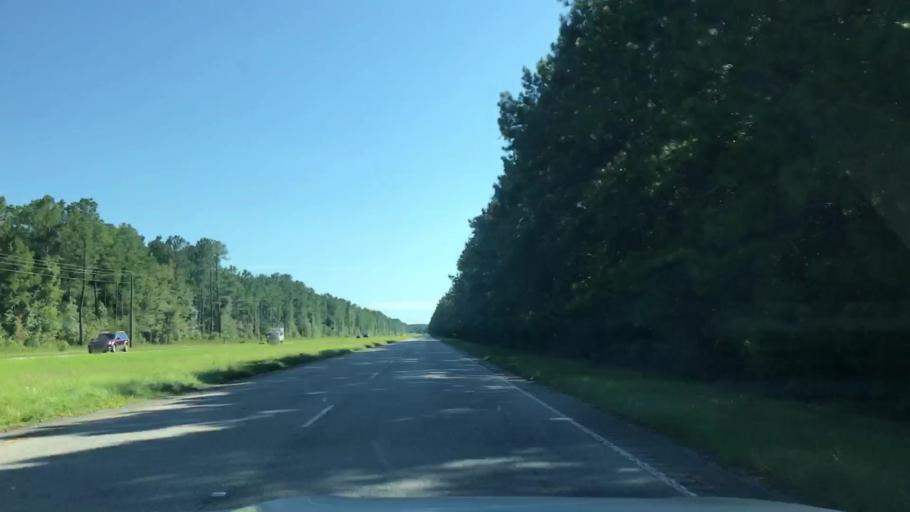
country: US
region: South Carolina
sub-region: Charleston County
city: Awendaw
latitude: 33.0210
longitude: -79.6324
